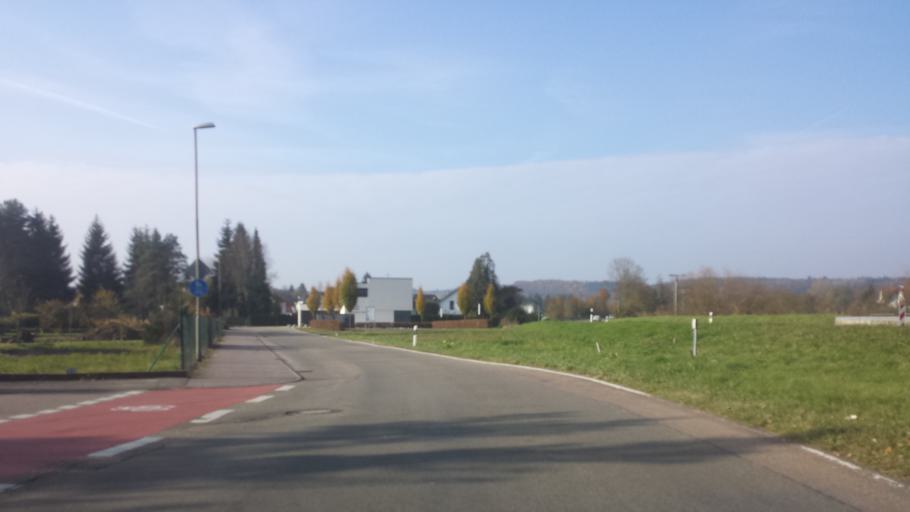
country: DE
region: Baden-Wuerttemberg
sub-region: Karlsruhe Region
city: Eschelbronn
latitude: 49.3197
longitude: 8.8740
